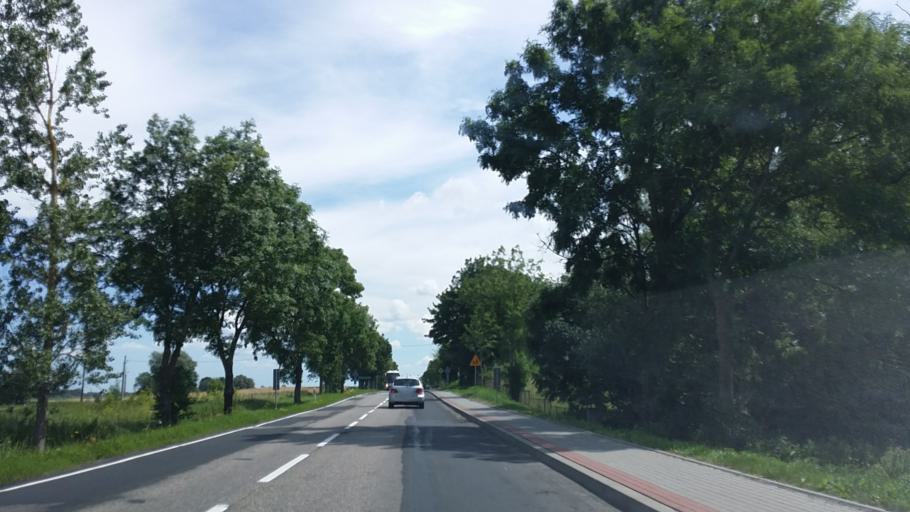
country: PL
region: West Pomeranian Voivodeship
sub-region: Powiat kolobrzeski
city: Ustronie Morskie
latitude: 54.2052
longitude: 15.8506
